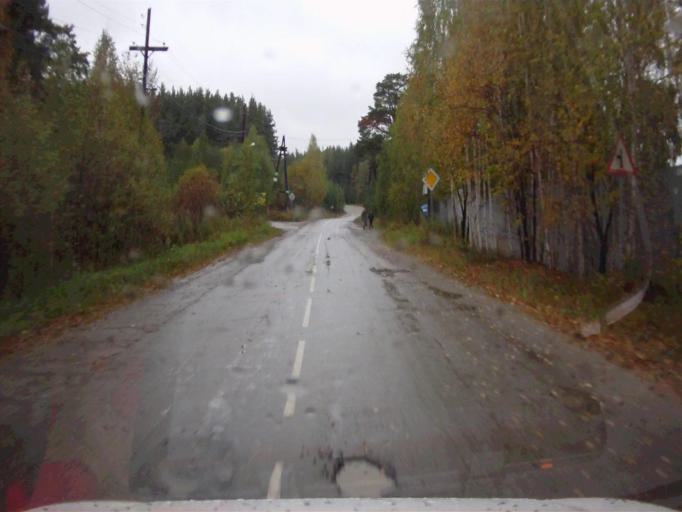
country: RU
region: Chelyabinsk
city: Kyshtym
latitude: 55.7448
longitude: 60.4921
